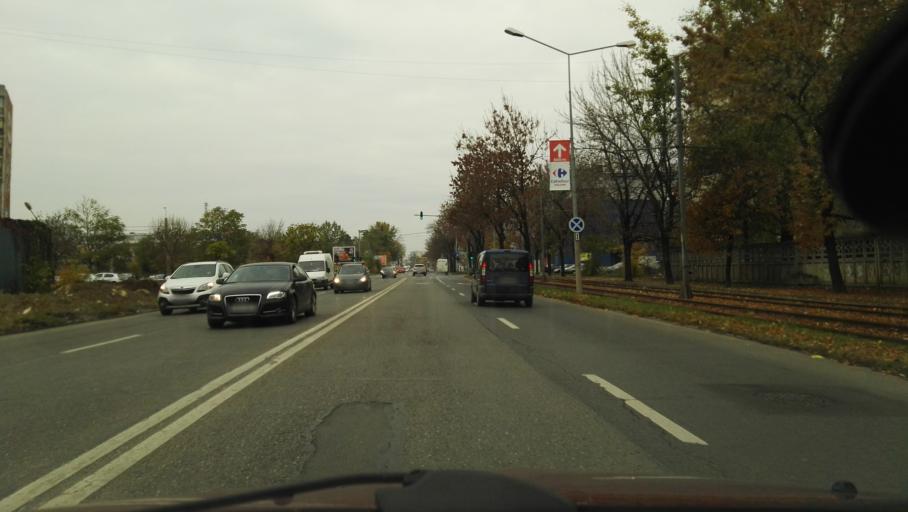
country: RO
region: Bucuresti
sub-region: Municipiul Bucuresti
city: Bucuresti
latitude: 44.4131
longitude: 26.0814
